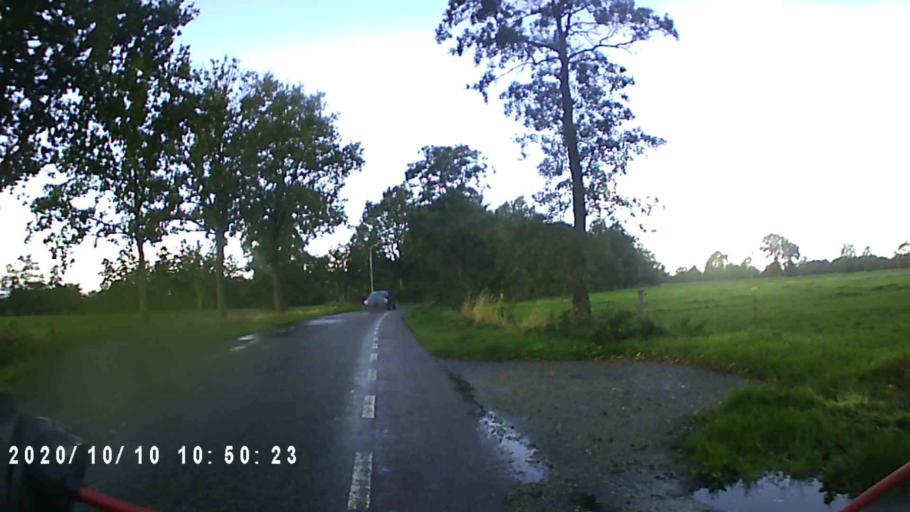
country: NL
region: Groningen
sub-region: Gemeente Grootegast
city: Grootegast
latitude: 53.1596
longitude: 6.2345
